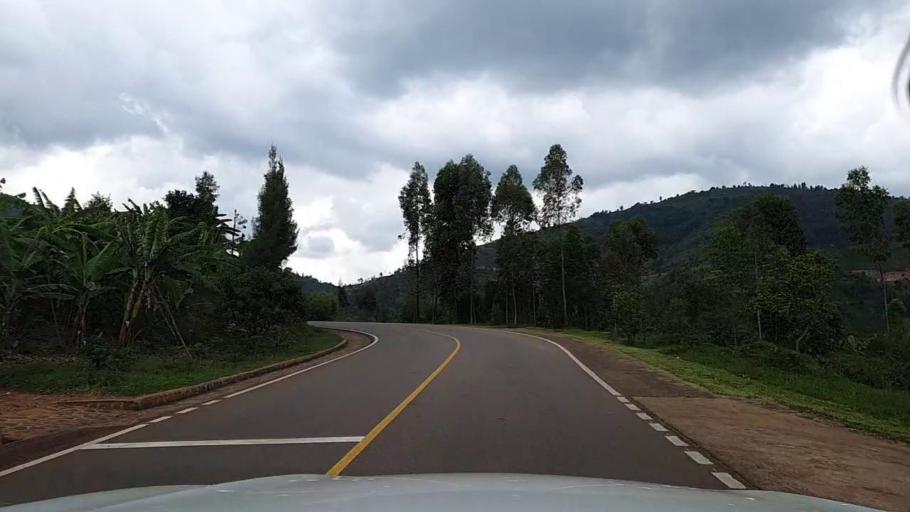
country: RW
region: Northern Province
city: Byumba
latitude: -1.6766
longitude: 30.0972
